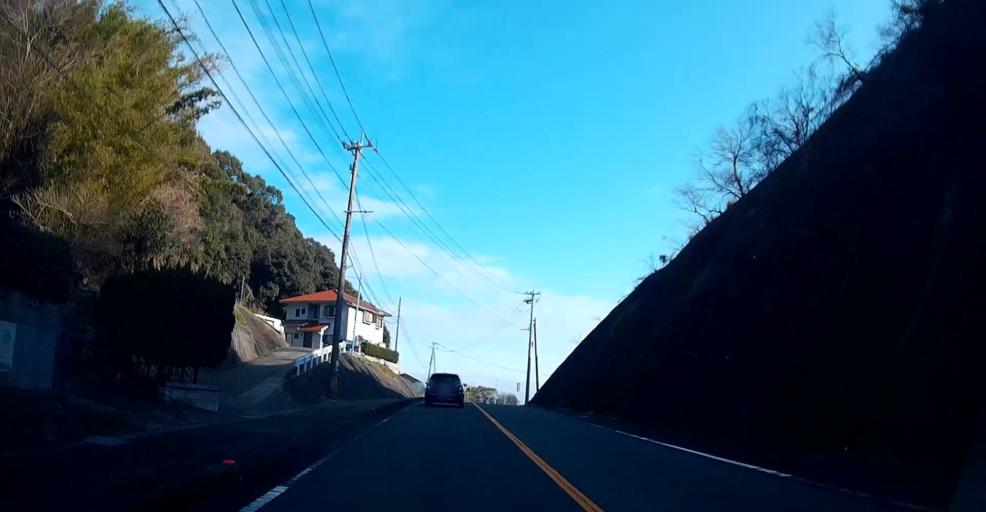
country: JP
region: Kumamoto
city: Yatsushiro
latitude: 32.5173
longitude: 130.4548
